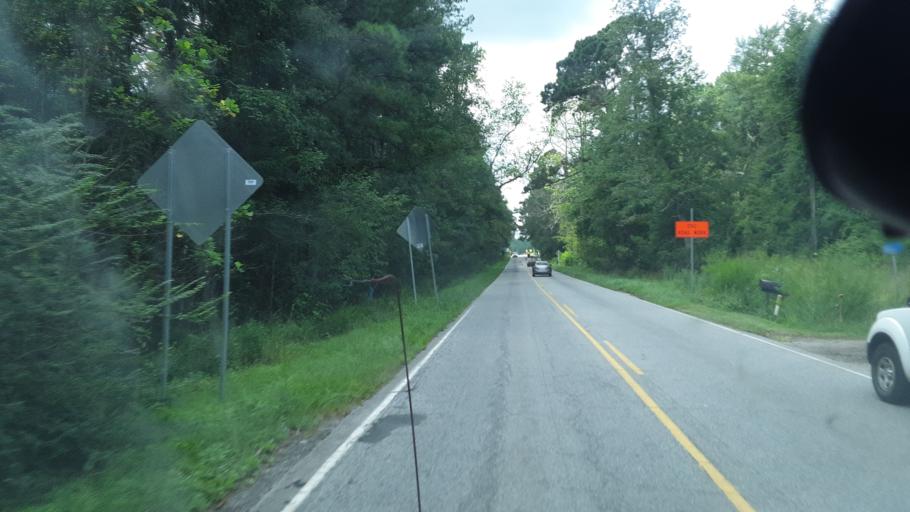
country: US
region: South Carolina
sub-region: Williamsburg County
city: Andrews
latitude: 33.3662
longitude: -79.4548
